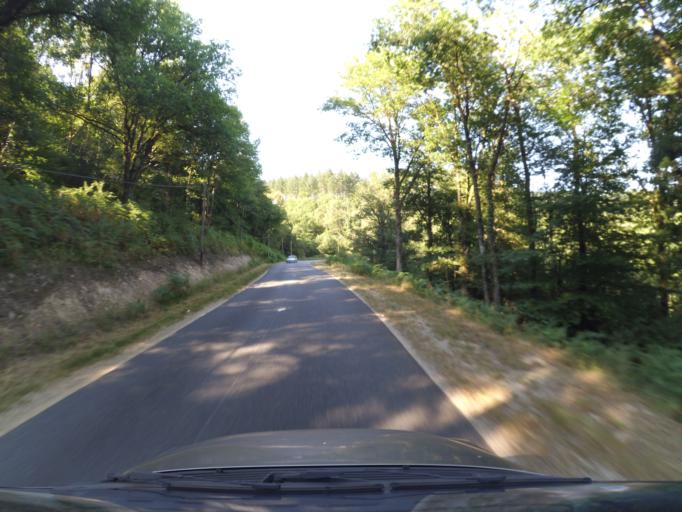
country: FR
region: Limousin
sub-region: Departement de la Haute-Vienne
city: Peyrat-le-Chateau
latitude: 45.7596
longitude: 1.8193
